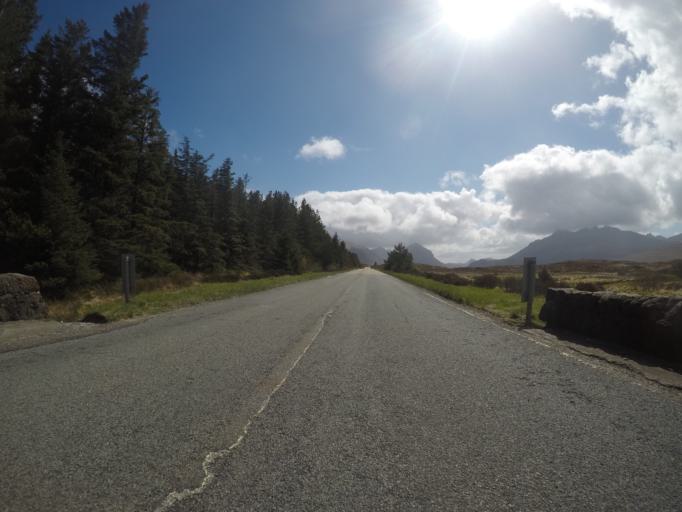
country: GB
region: Scotland
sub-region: Highland
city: Isle of Skye
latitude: 57.3128
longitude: -6.1972
